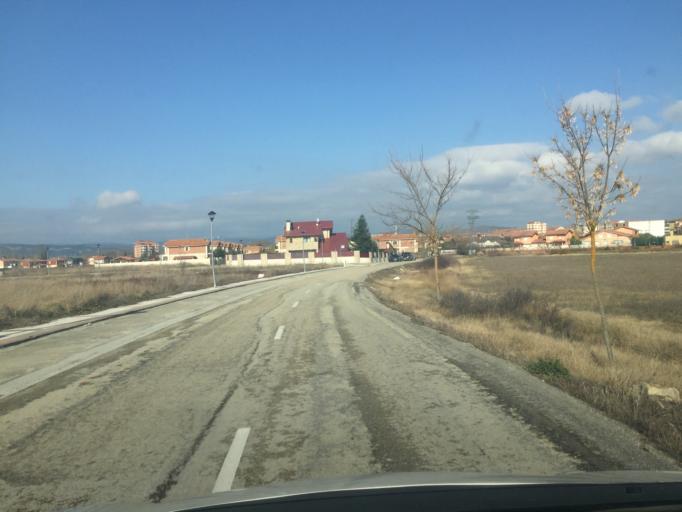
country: ES
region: Castille and Leon
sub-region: Provincia de Burgos
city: Medina de Pomar
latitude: 42.9310
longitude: -3.5789
